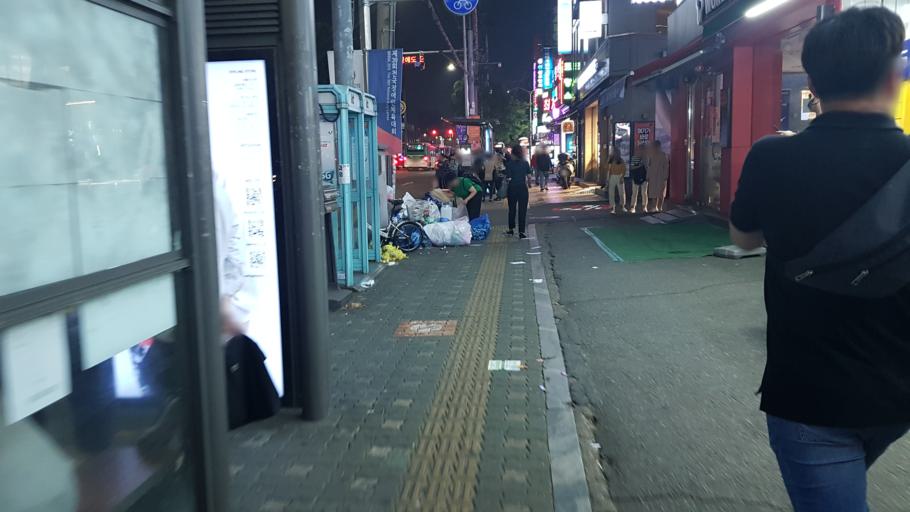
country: KR
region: Gyeonggi-do
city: Kwangmyong
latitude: 37.4842
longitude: 126.9284
